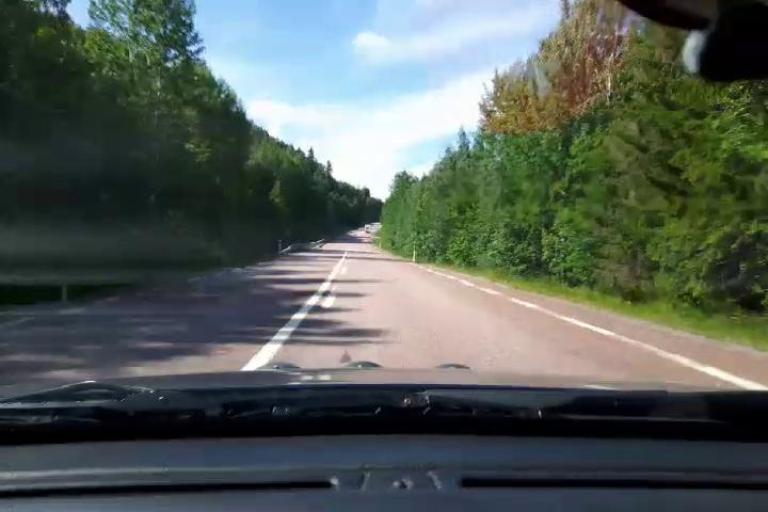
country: SE
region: Gaevleborg
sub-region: Bollnas Kommun
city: Kilafors
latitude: 61.1963
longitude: 16.7647
